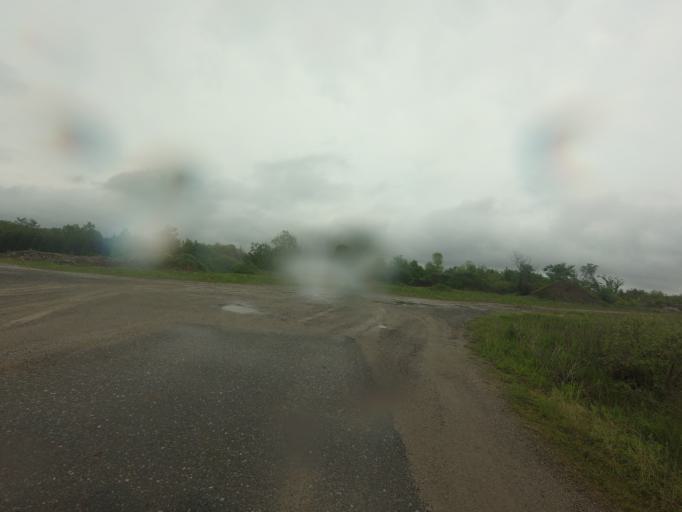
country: CA
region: Ontario
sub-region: Lanark County
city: Smiths Falls
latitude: 44.8712
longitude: -76.0417
